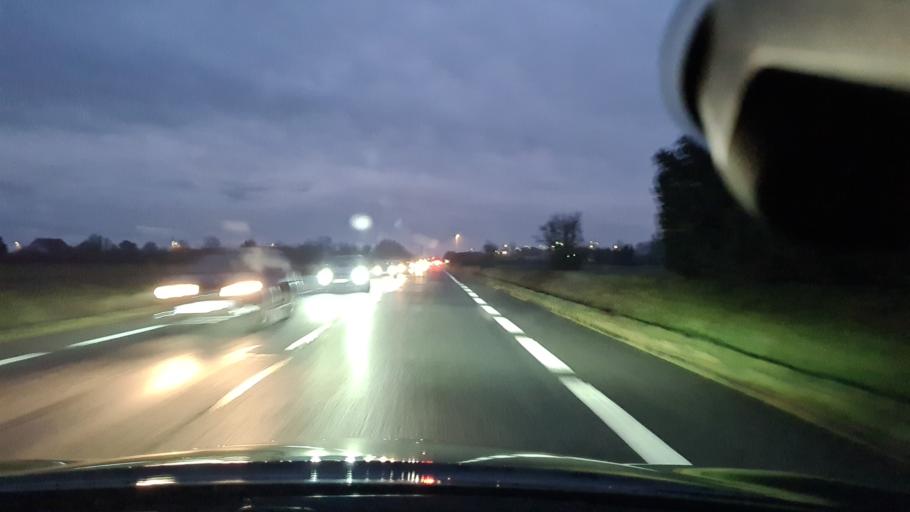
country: FR
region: Rhone-Alpes
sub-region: Departement du Rhone
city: Genas
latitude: 45.7456
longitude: 5.0218
